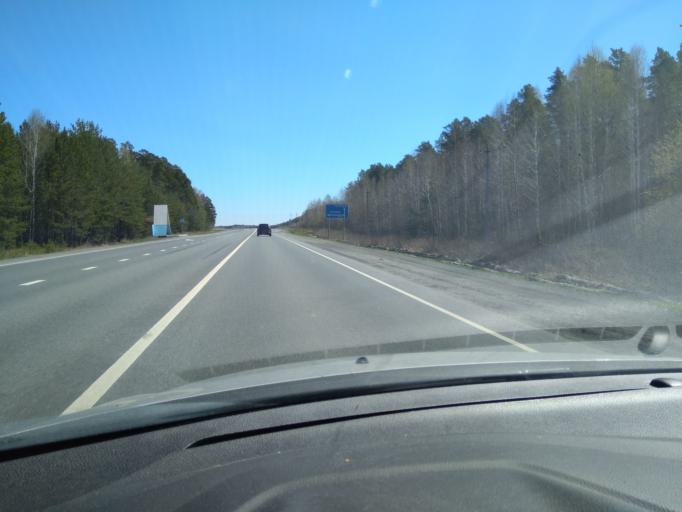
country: RU
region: Sverdlovsk
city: Troitskiy
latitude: 57.0888
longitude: 63.8735
